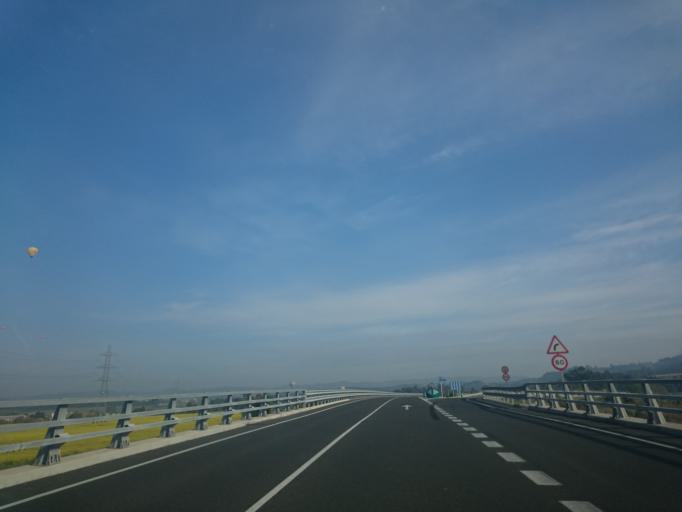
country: ES
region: Catalonia
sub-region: Provincia de Barcelona
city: Odena
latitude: 41.5891
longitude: 1.6630
